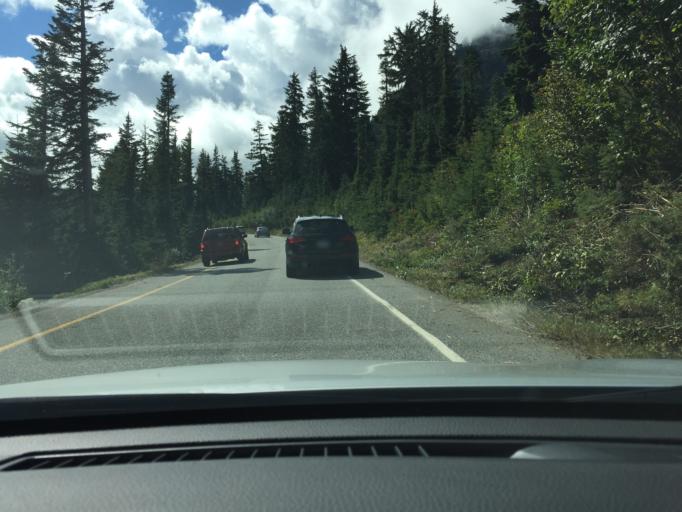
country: CA
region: British Columbia
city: Agassiz
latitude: 48.8664
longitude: -121.6785
